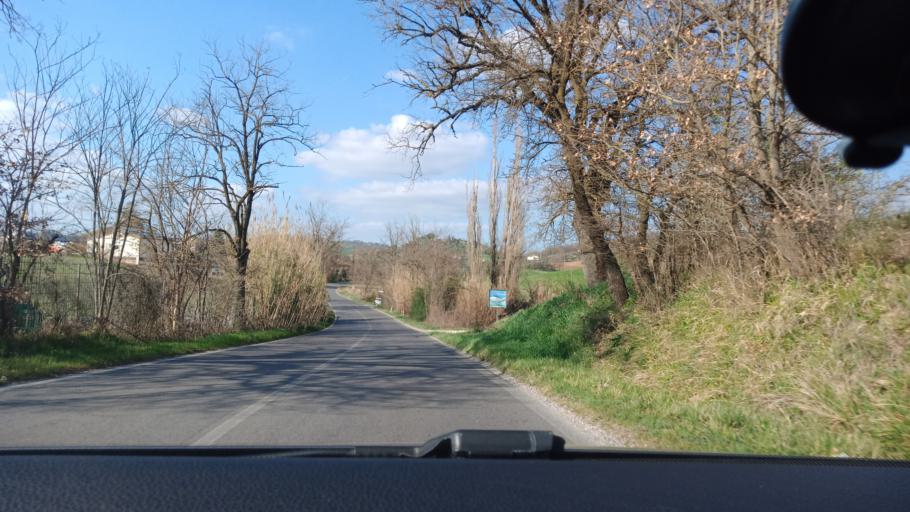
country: IT
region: Latium
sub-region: Citta metropolitana di Roma Capitale
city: Torrita Tiberina
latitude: 42.2577
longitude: 12.6394
